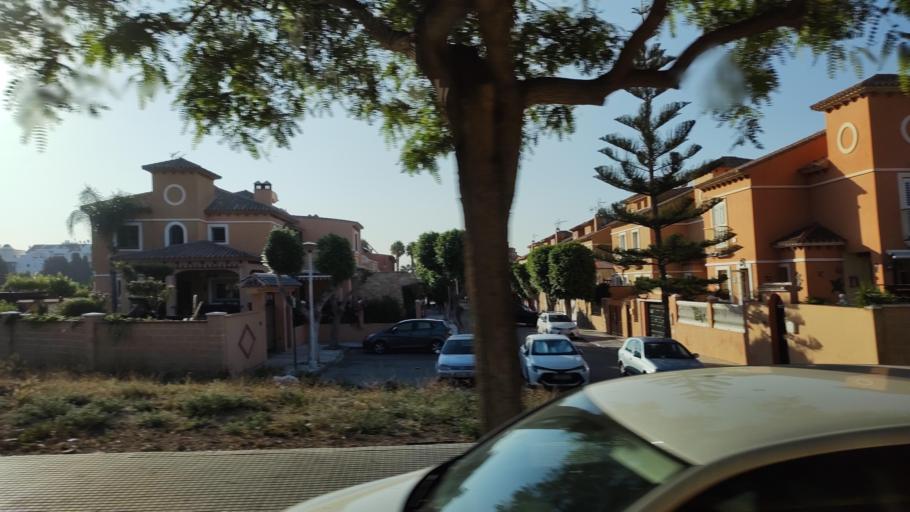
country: ES
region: Andalusia
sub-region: Provincia de Malaga
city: Torremolinos
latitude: 36.6411
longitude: -4.4872
